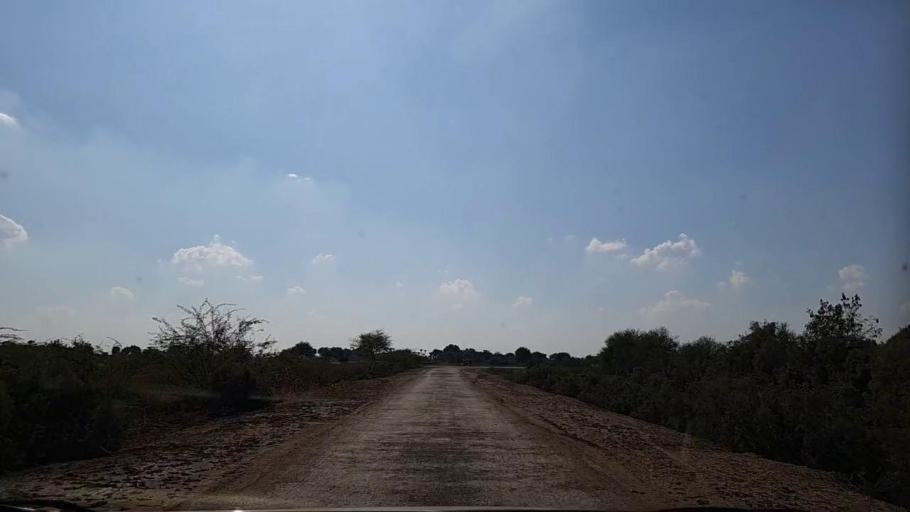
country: PK
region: Sindh
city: Pithoro
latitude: 25.6698
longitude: 69.4767
